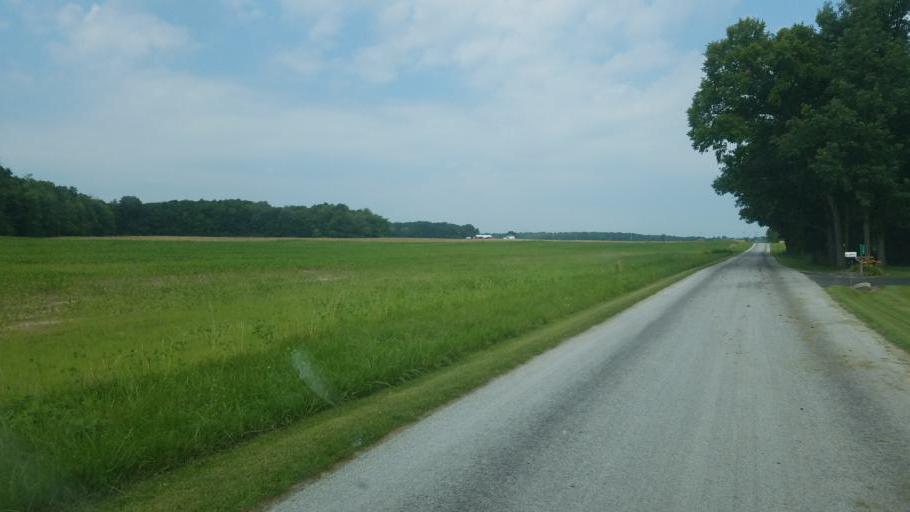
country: US
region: Ohio
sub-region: Hardin County
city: Kenton
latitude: 40.5799
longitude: -83.5123
